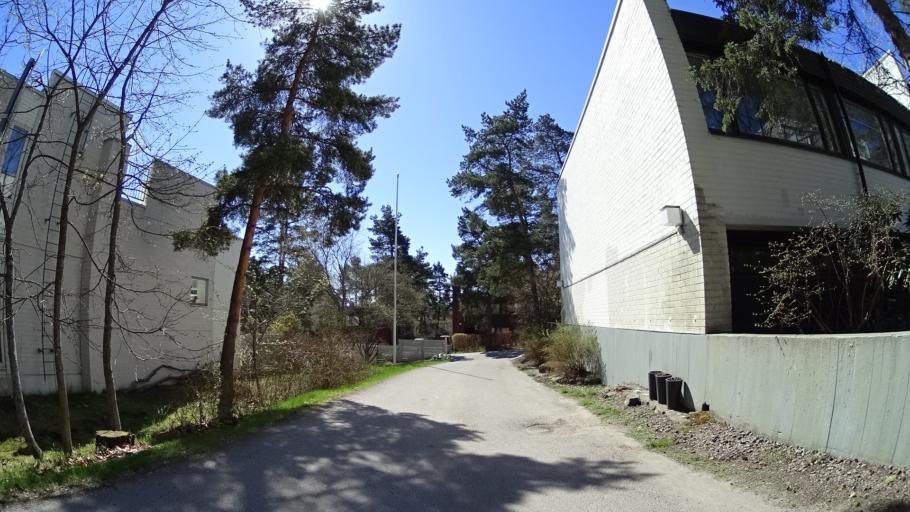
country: FI
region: Uusimaa
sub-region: Helsinki
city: Koukkuniemi
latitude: 60.1586
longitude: 24.7799
